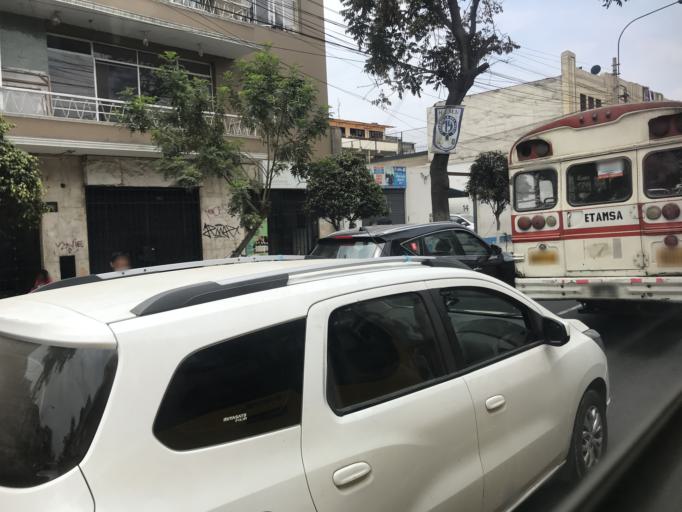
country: PE
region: Lima
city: Lima
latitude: -12.0563
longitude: -77.0434
